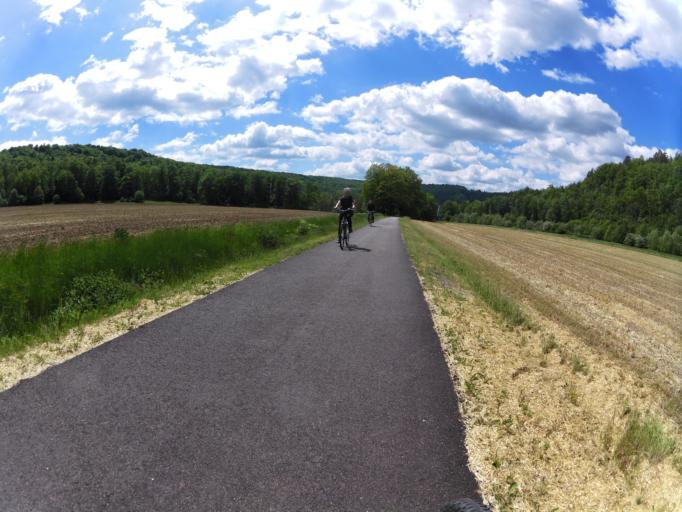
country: DE
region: Thuringia
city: Ebenshausen
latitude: 51.0922
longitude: 10.2960
